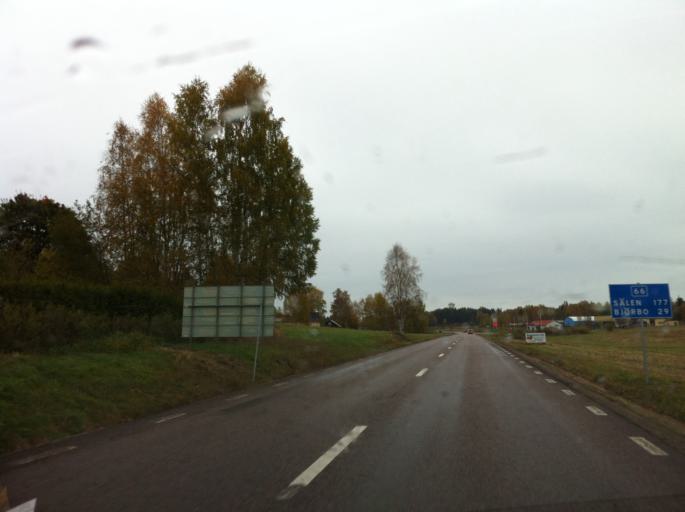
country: SE
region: Dalarna
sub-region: Ludvika Kommun
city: Grangesberg
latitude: 60.2517
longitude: 14.9798
